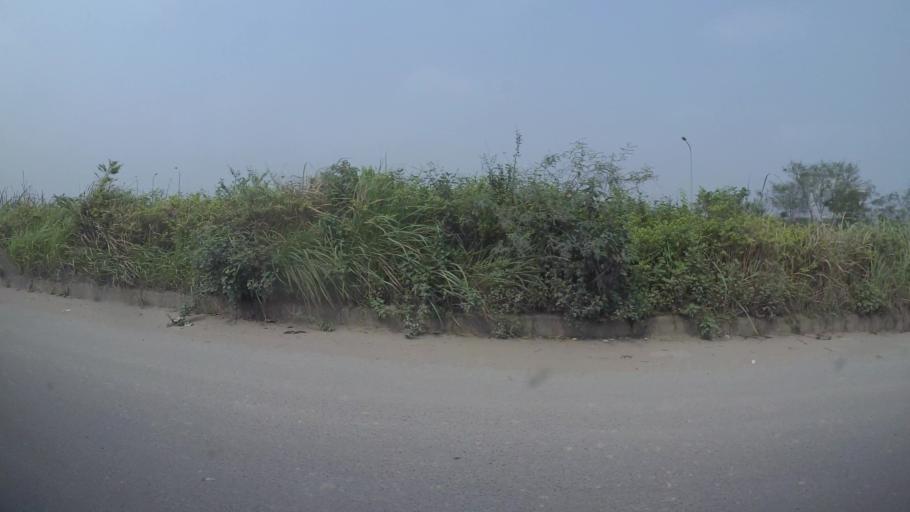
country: VN
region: Ha Noi
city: Cau Dien
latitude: 21.0105
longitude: 105.7490
